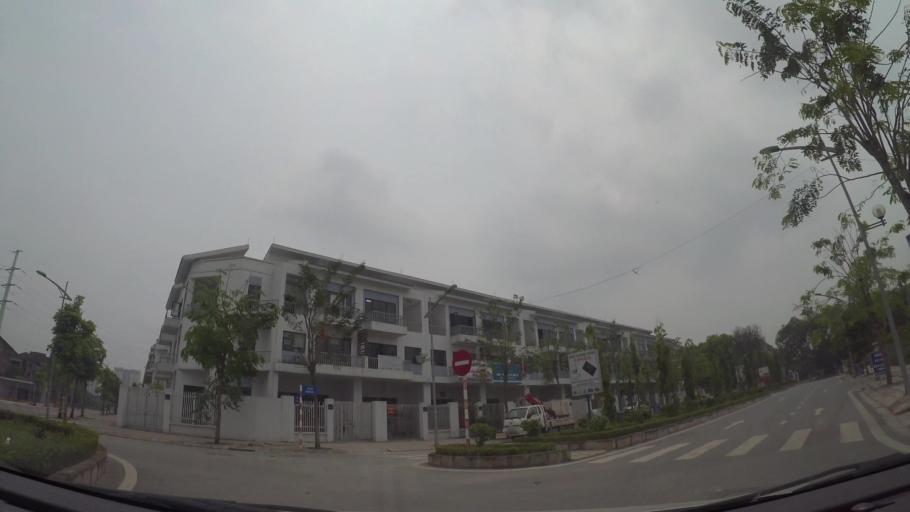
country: VN
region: Ha Noi
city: Cau Dien
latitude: 21.0264
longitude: 105.7425
